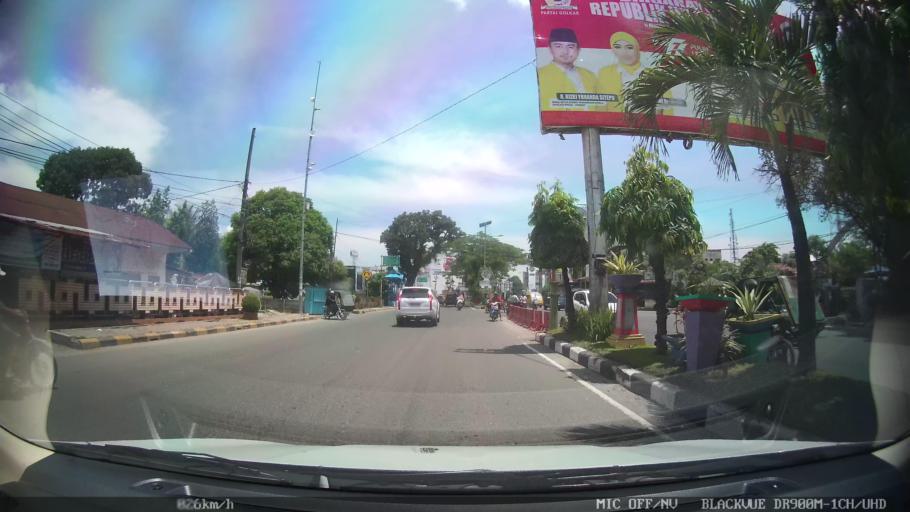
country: ID
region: North Sumatra
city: Binjai
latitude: 3.6088
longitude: 98.4947
